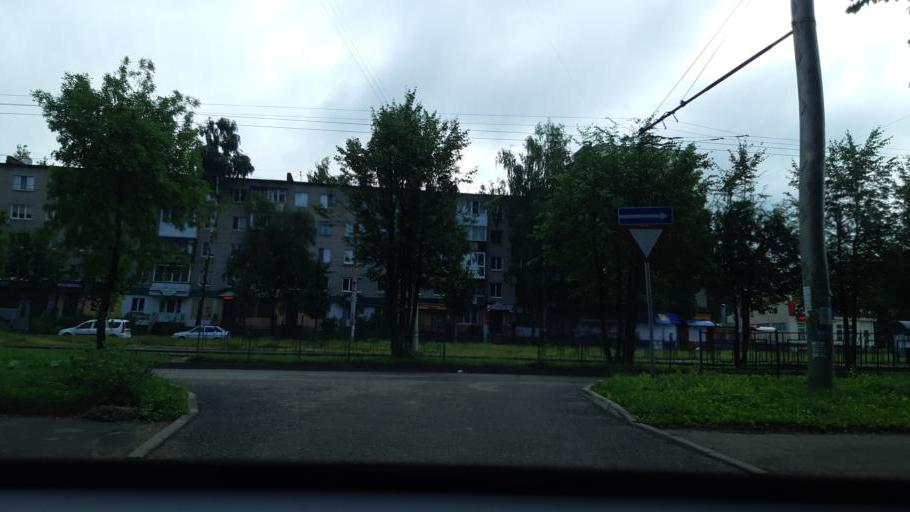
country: RU
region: Smolensk
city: Smolensk
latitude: 54.7654
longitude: 32.0906
